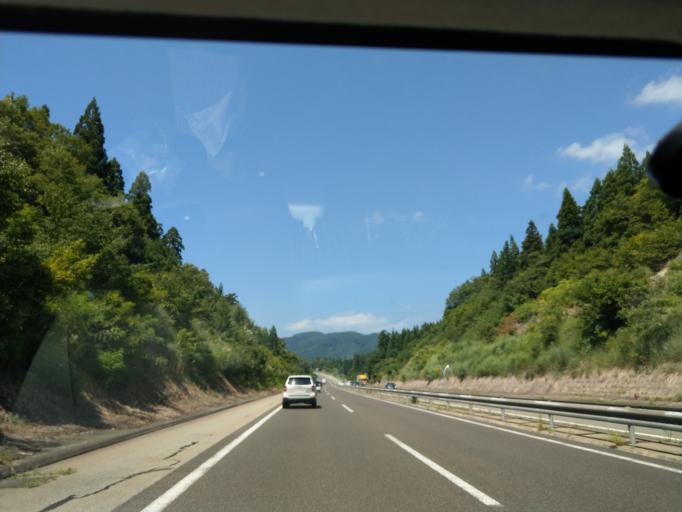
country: JP
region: Akita
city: Omagari
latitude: 39.4155
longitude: 140.4373
